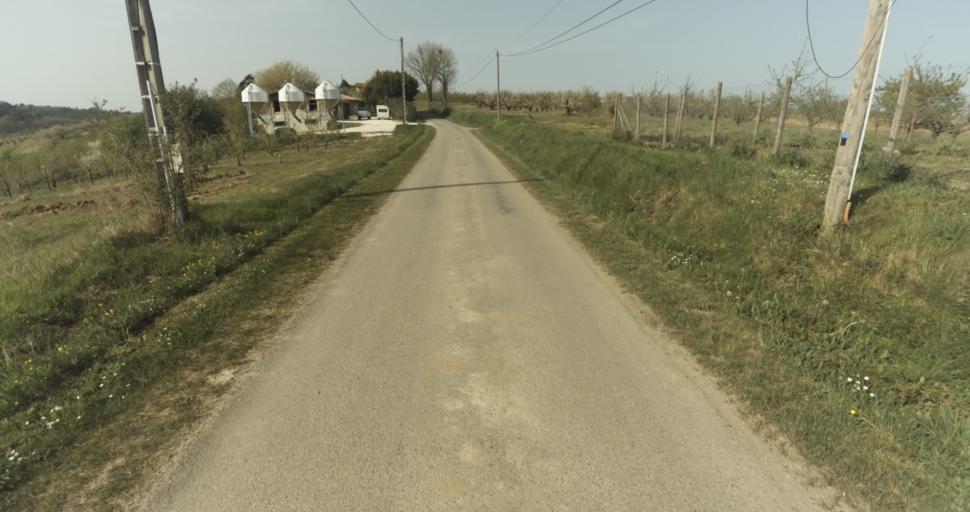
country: FR
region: Midi-Pyrenees
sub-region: Departement du Tarn-et-Garonne
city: Lafrancaise
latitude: 44.1416
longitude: 1.1647
